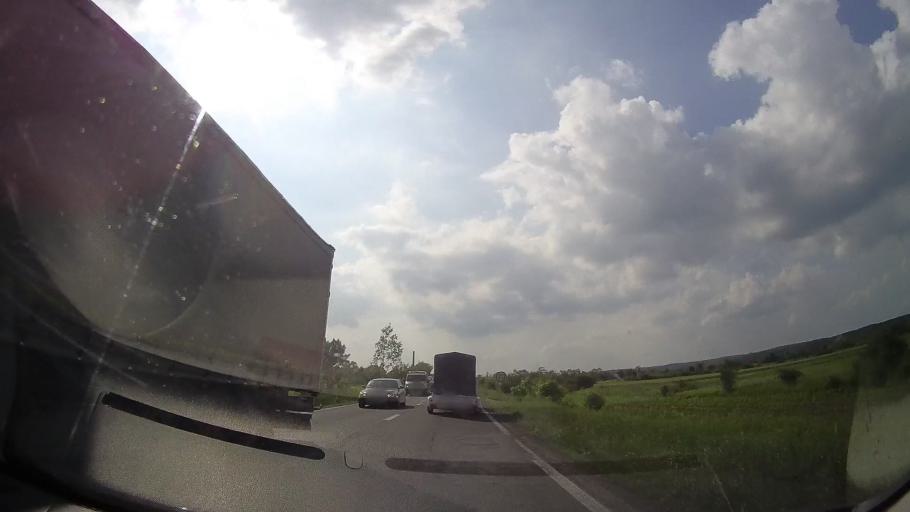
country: RO
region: Timis
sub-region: Comuna Margina
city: Margina
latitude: 45.8559
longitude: 22.2763
